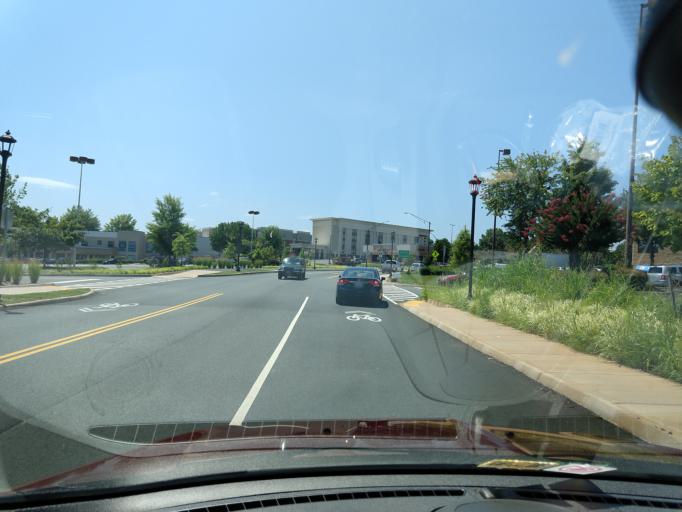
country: US
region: Virginia
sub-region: City of Charlottesville
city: Charlottesville
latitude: 38.0645
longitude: -78.4874
